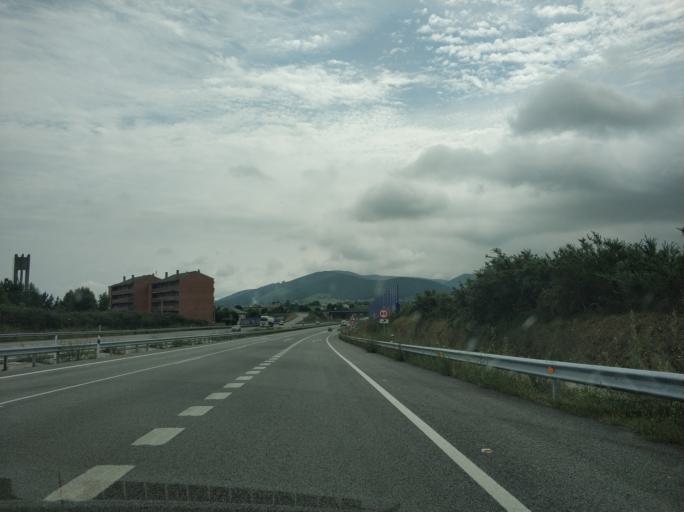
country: ES
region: Asturias
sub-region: Province of Asturias
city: Navia
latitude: 43.5284
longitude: -6.5570
